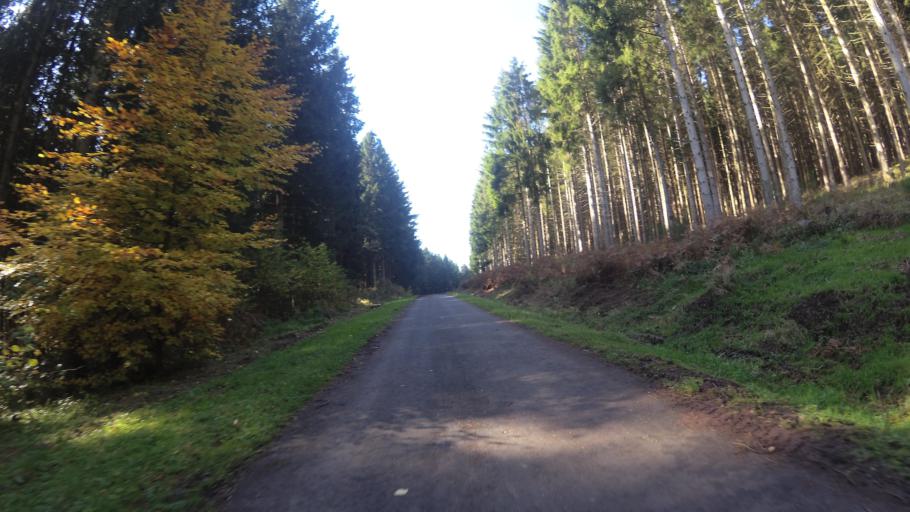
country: DE
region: Rheinland-Pfalz
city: Mandern
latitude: 49.6125
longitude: 6.7513
